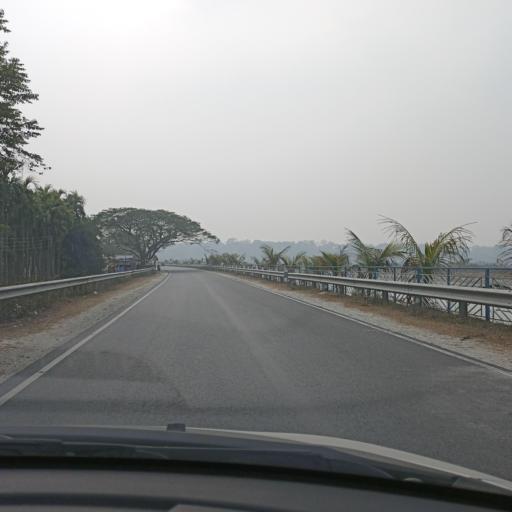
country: IN
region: West Bengal
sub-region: Jalpaiguri
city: Odlabari
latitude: 26.7432
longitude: 88.5773
